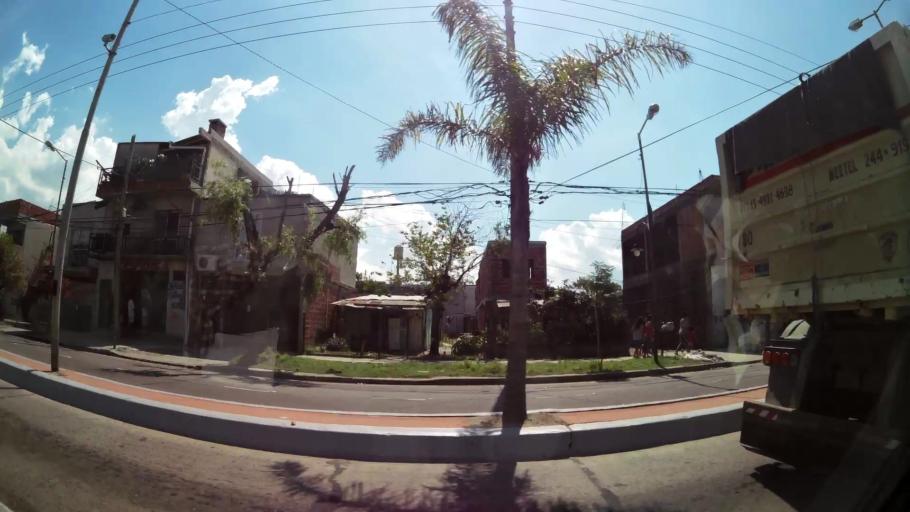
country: AR
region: Buenos Aires
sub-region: Partido de Tigre
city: Tigre
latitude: -34.4726
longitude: -58.5972
